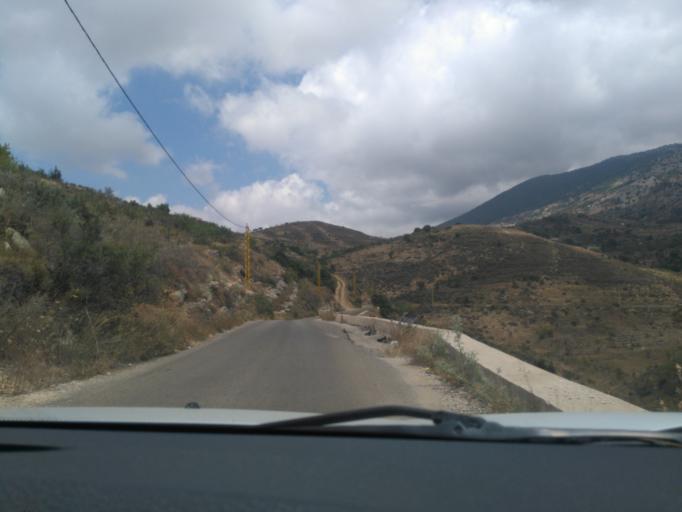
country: LB
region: Mont-Liban
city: Beit ed Dine
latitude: 33.6760
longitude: 35.6657
